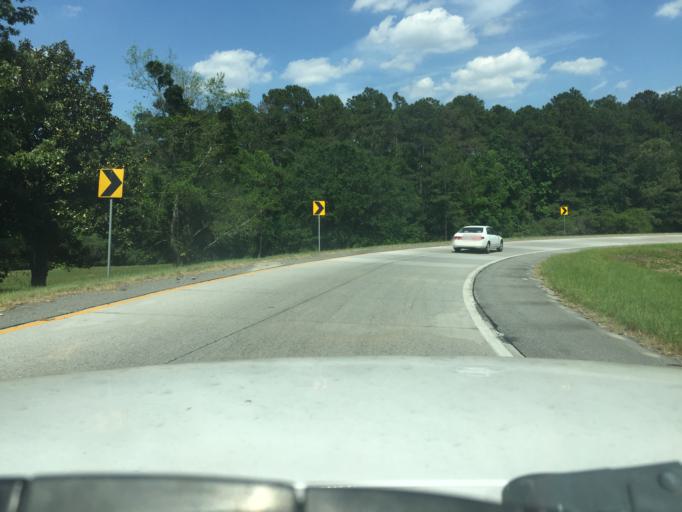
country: US
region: Georgia
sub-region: Chatham County
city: Pooler
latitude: 32.0754
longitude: -81.2449
